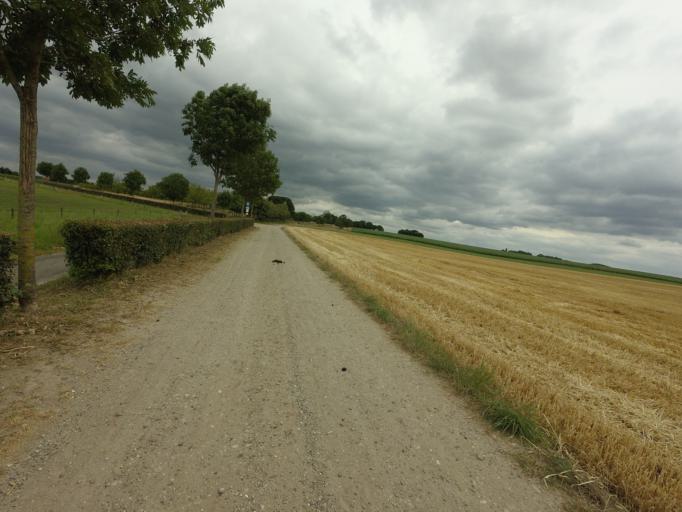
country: NL
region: Limburg
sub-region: Valkenburg aan de Geul
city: Sibbe
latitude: 50.8377
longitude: 5.8227
